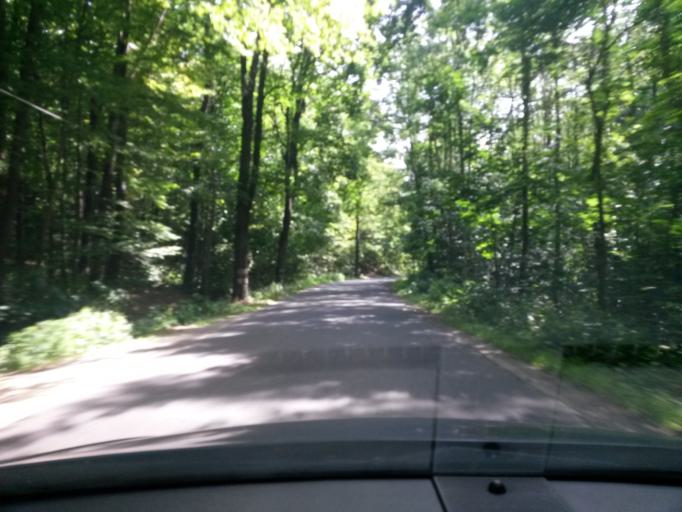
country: PL
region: Lower Silesian Voivodeship
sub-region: Powiat jaworski
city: Paszowice
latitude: 51.0065
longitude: 16.1307
